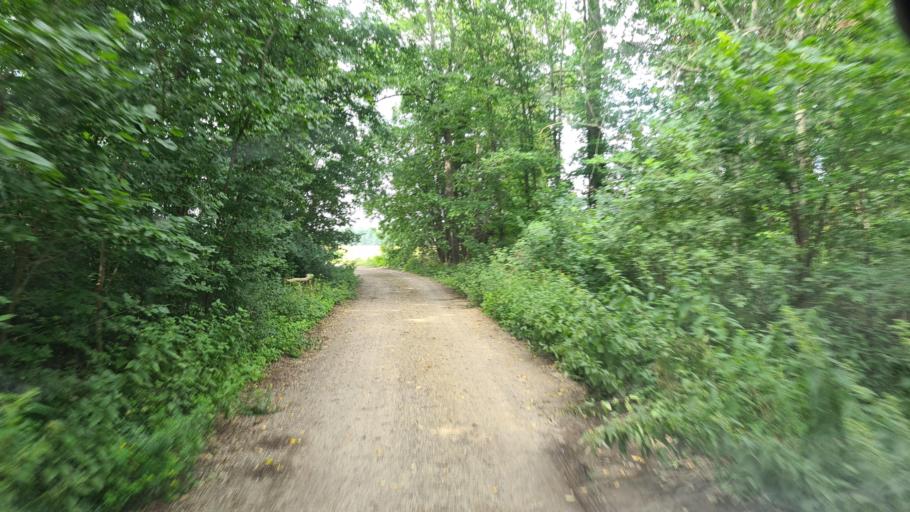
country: DE
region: Brandenburg
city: Bronkow
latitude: 51.6119
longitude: 13.9024
